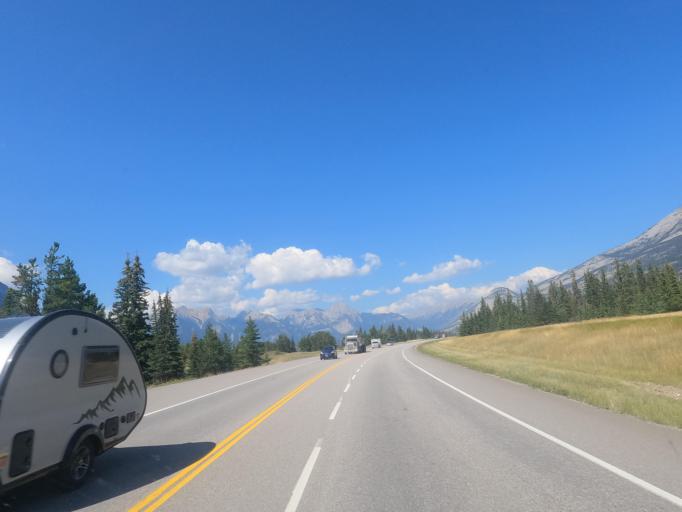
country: CA
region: Alberta
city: Jasper Park Lodge
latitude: 52.9693
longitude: -118.0565
